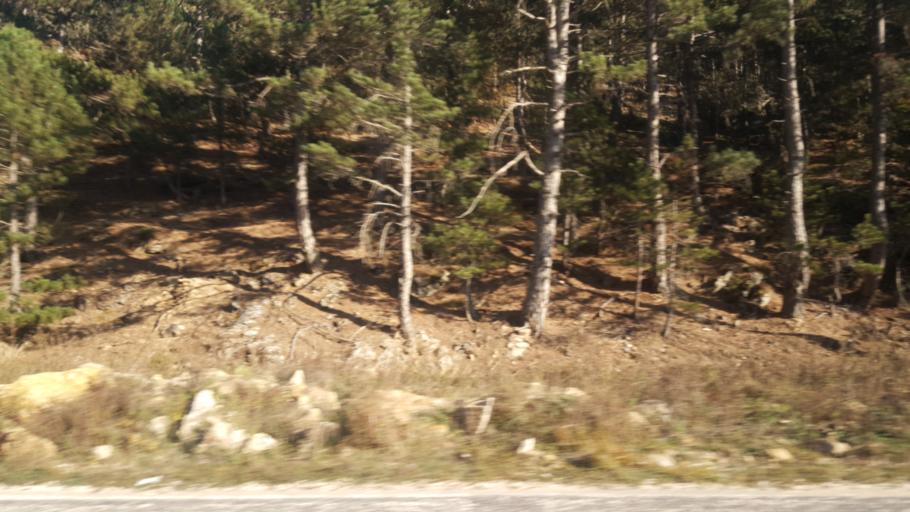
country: TR
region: Afyonkarahisar
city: Ihsaniye
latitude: 39.1038
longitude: 30.5810
